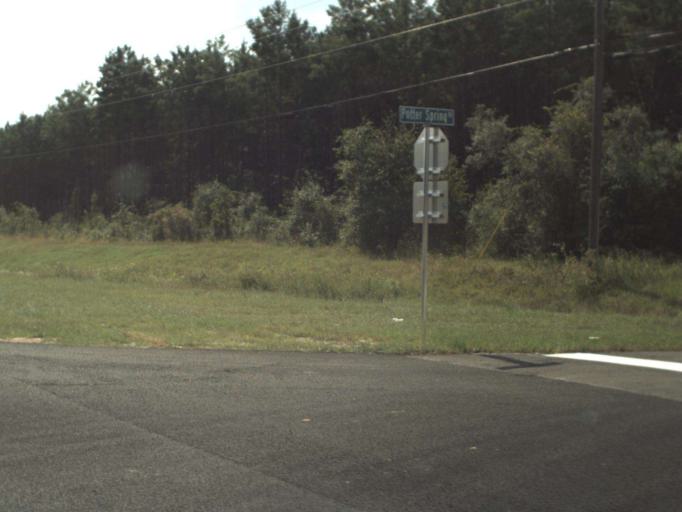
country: US
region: Florida
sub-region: Holmes County
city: Bonifay
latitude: 30.5345
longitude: -85.8360
